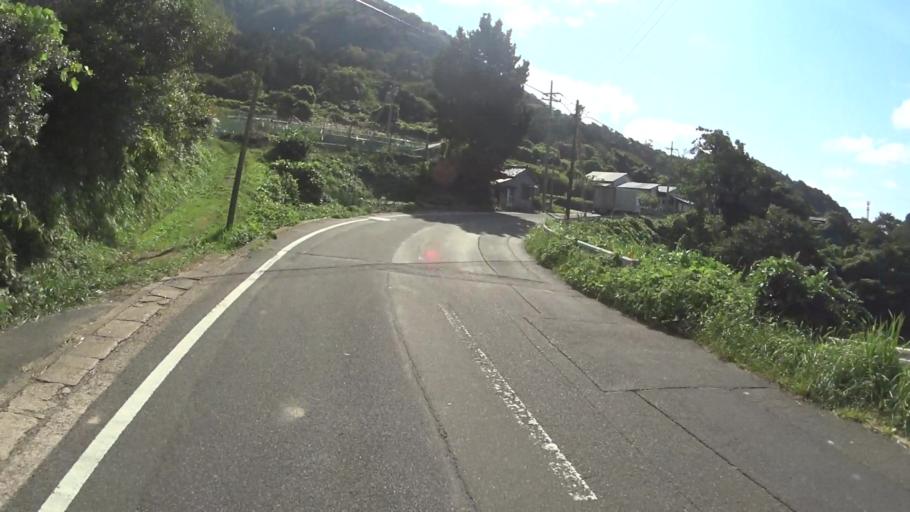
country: JP
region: Kyoto
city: Miyazu
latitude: 35.7643
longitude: 135.1992
